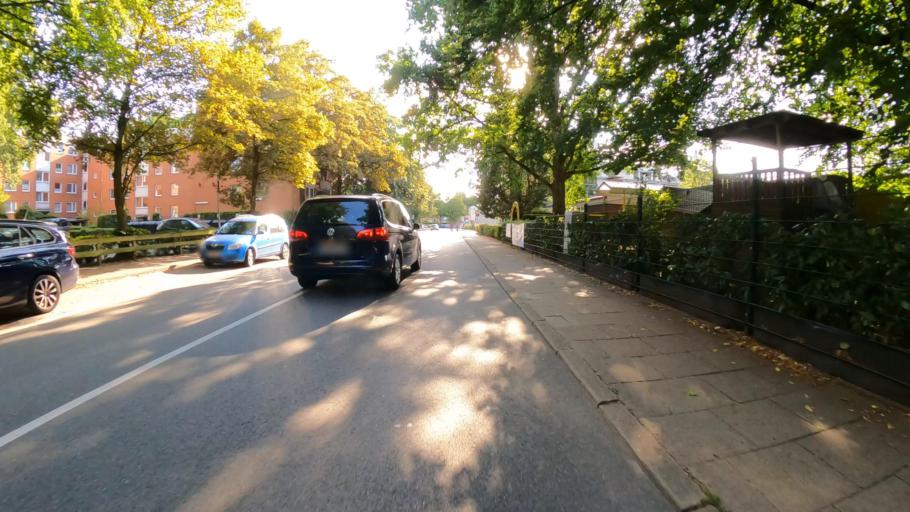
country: DE
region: Schleswig-Holstein
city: Stapelfeld
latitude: 53.6274
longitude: 10.1707
